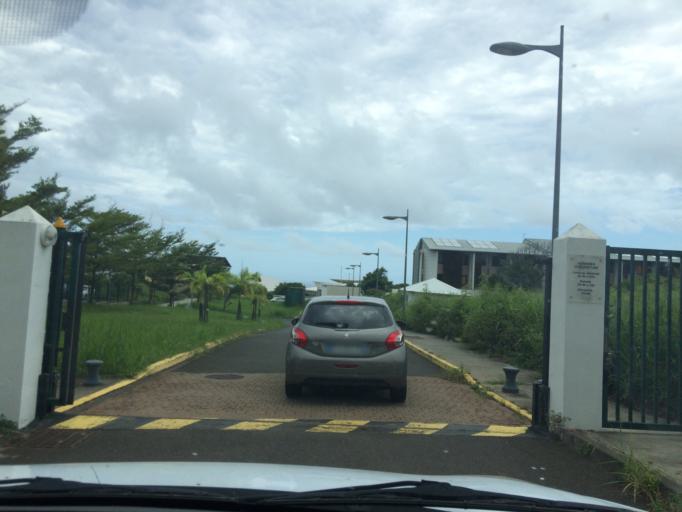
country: RE
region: Reunion
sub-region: Reunion
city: Saint-Pierre
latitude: -21.3396
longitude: 55.4909
